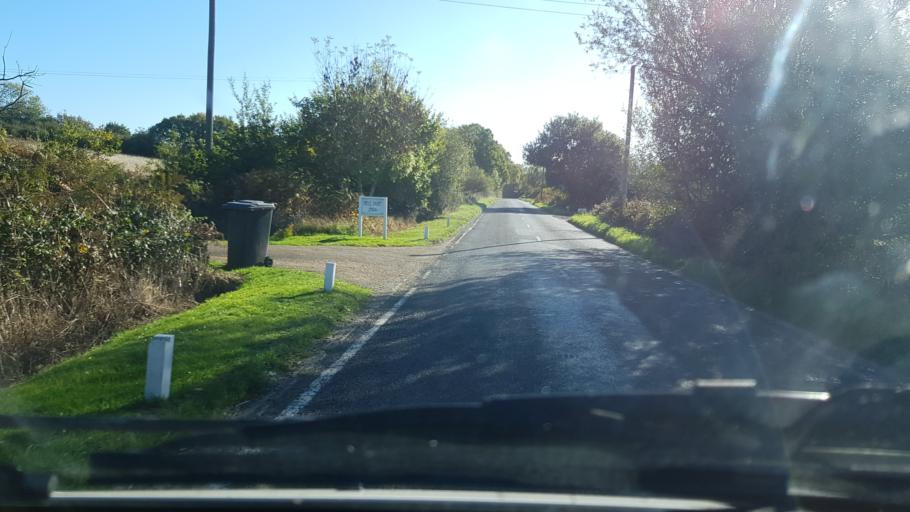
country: GB
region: England
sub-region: Surrey
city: Cranleigh
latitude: 51.1606
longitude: -0.4971
